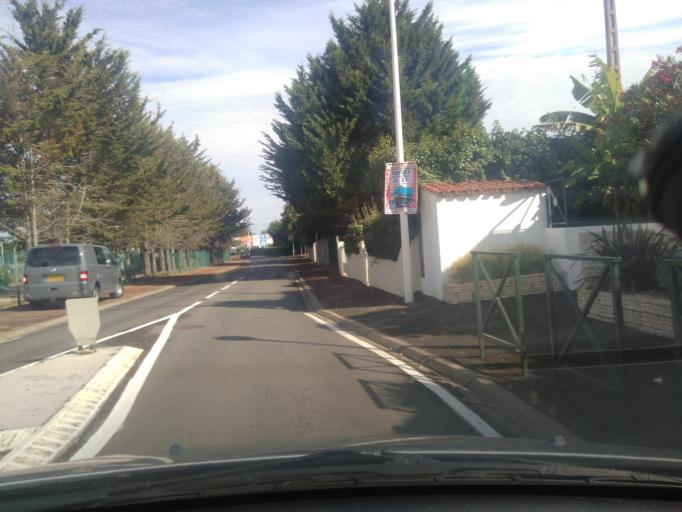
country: FR
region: Pays de la Loire
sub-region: Departement de la Vendee
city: Olonne-sur-Mer
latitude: 46.5317
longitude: -1.7585
